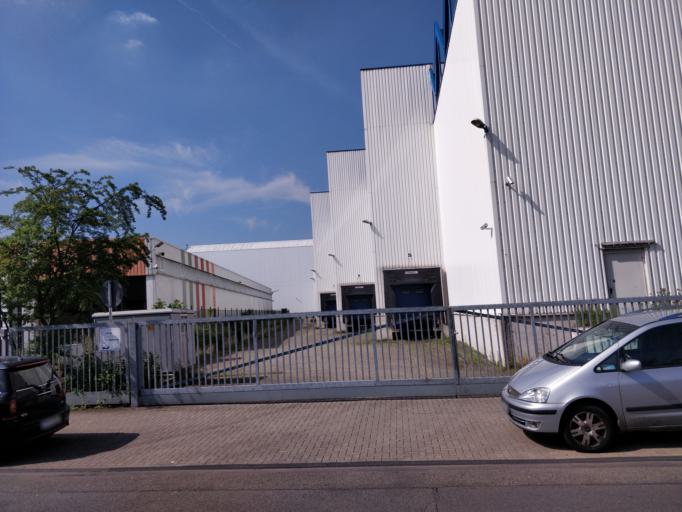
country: DE
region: North Rhine-Westphalia
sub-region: Regierungsbezirk Koln
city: Mengenich
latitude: 50.9860
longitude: 6.8871
